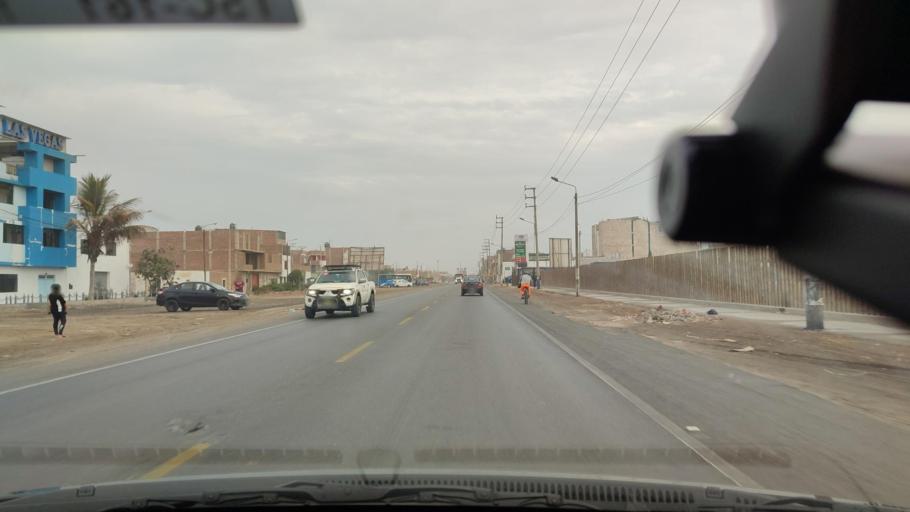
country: PE
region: La Libertad
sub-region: Provincia de Trujillo
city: Buenos Aires
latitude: -8.1456
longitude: -79.0467
